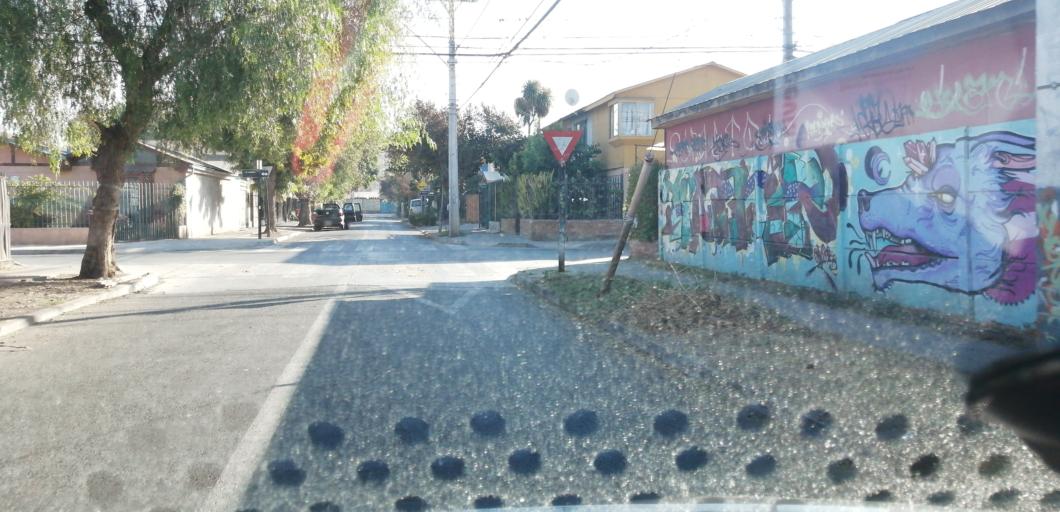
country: CL
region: Santiago Metropolitan
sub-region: Provincia de Santiago
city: Lo Prado
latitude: -33.4588
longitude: -70.7420
